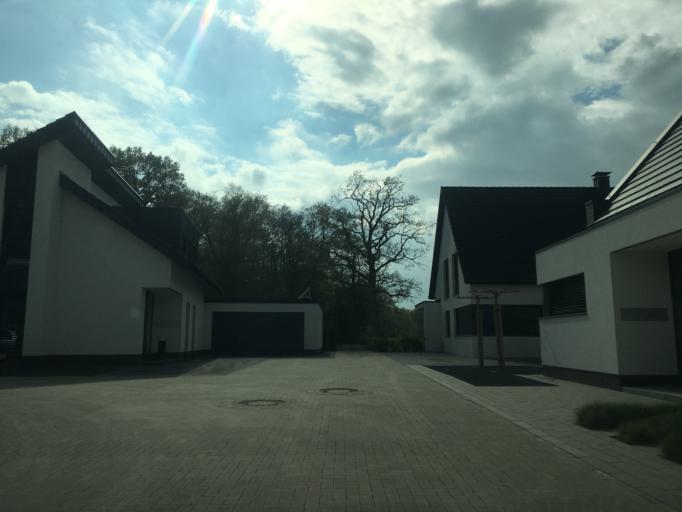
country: DE
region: North Rhine-Westphalia
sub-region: Regierungsbezirk Munster
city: Steinfurt
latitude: 52.1333
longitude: 7.3368
